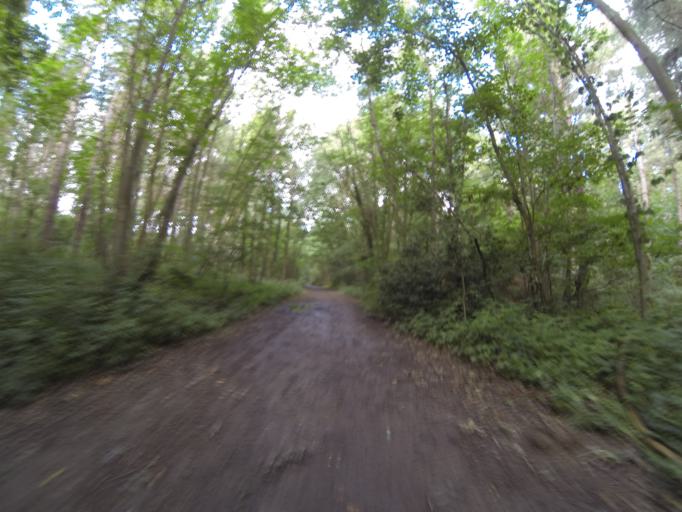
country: GB
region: England
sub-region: Greater London
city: Bexley
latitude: 51.4290
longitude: 0.1592
